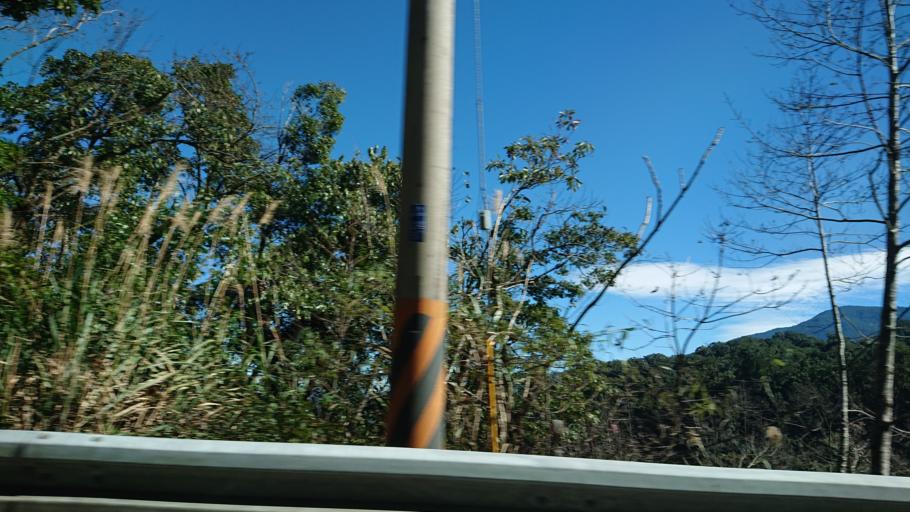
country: TW
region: Taiwan
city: Daxi
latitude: 24.4062
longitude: 121.3605
